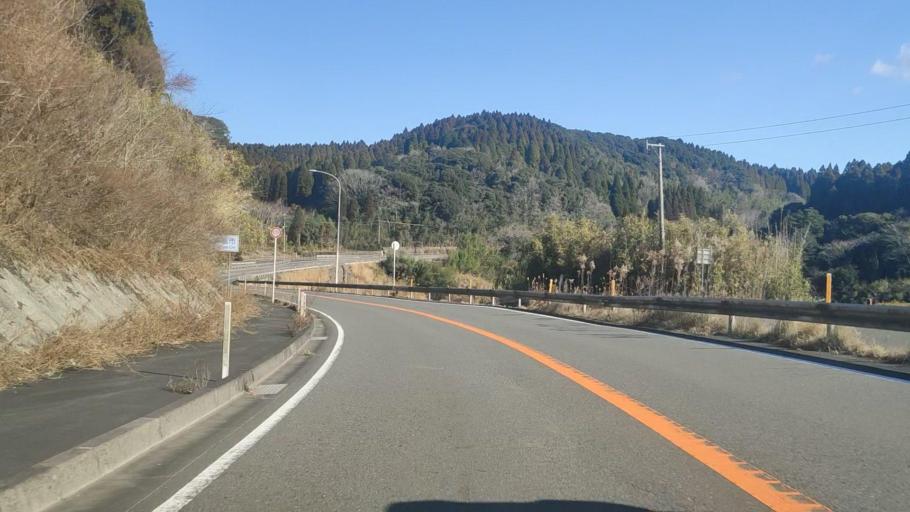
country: JP
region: Kagoshima
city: Sueyoshicho-ninokata
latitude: 31.6613
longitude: 130.8969
